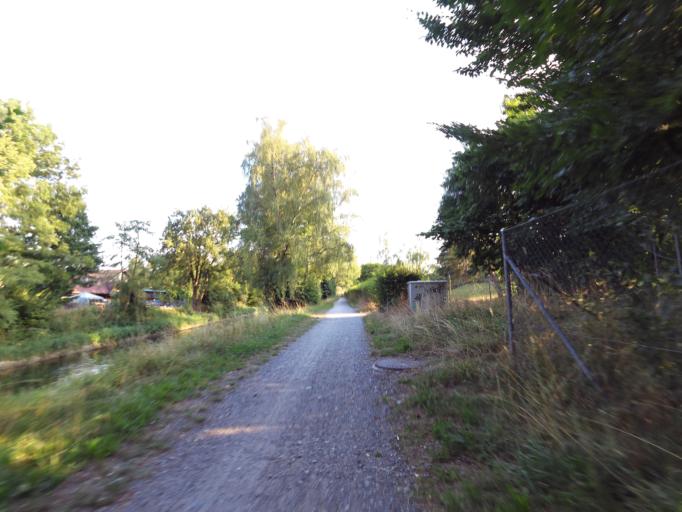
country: CH
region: Zurich
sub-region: Bezirk Zuerich
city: Zuerich (Kreis 12) / Auzelg
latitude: 47.4182
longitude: 8.5673
